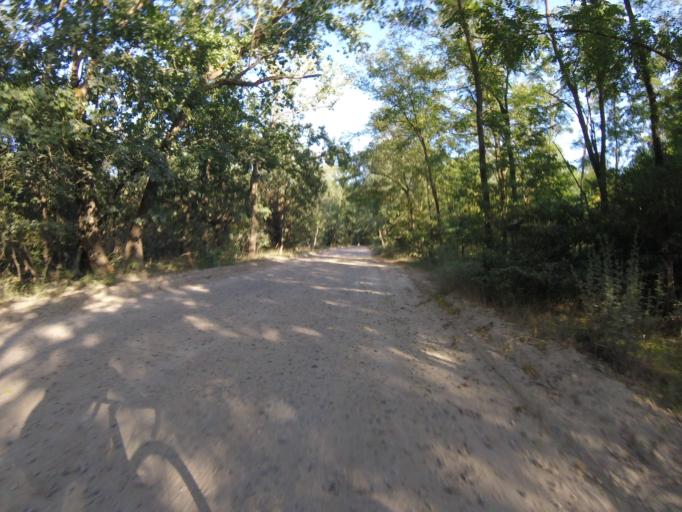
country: DE
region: Brandenburg
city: Zossen
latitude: 52.2015
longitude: 13.4994
